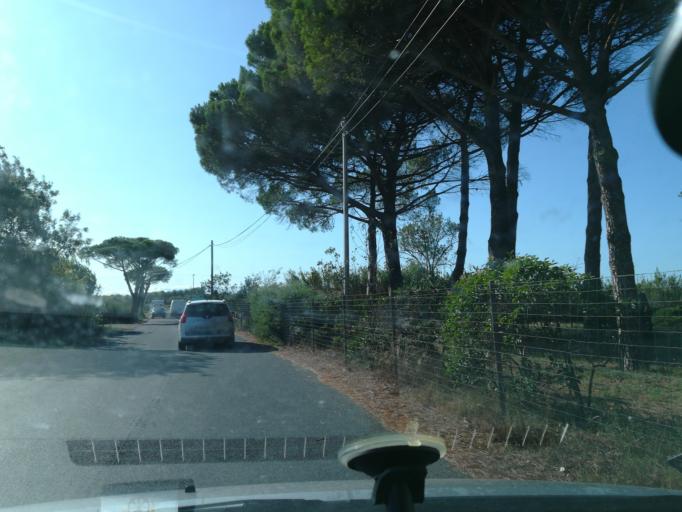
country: FR
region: Languedoc-Roussillon
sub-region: Departement de l'Herault
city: Portiragnes
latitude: 43.2874
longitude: 3.3709
